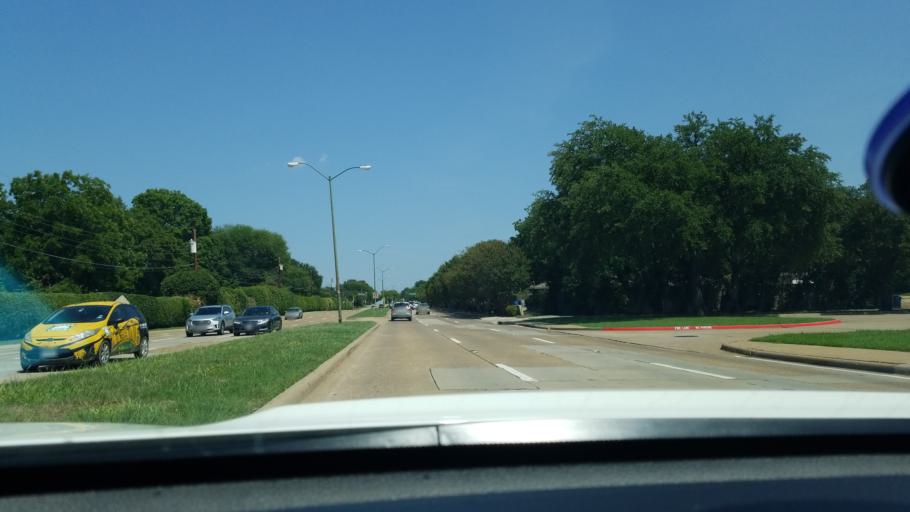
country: US
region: Texas
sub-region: Dallas County
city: Richardson
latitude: 32.9620
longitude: -96.7764
